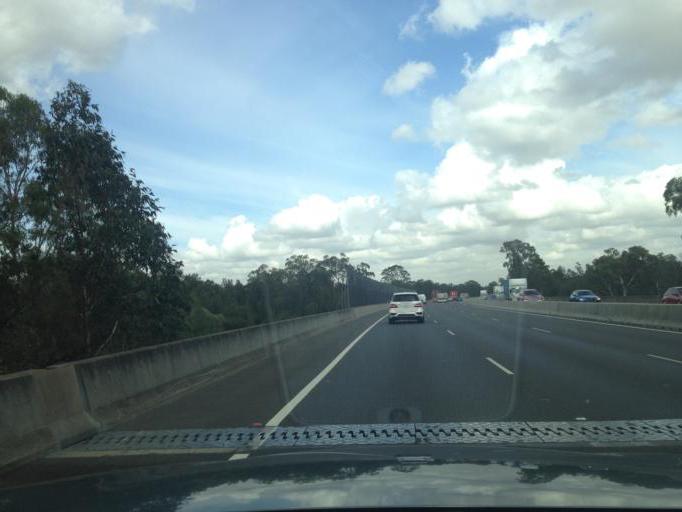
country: AU
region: New South Wales
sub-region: Bankstown
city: Milperra
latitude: -33.9465
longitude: 150.9723
